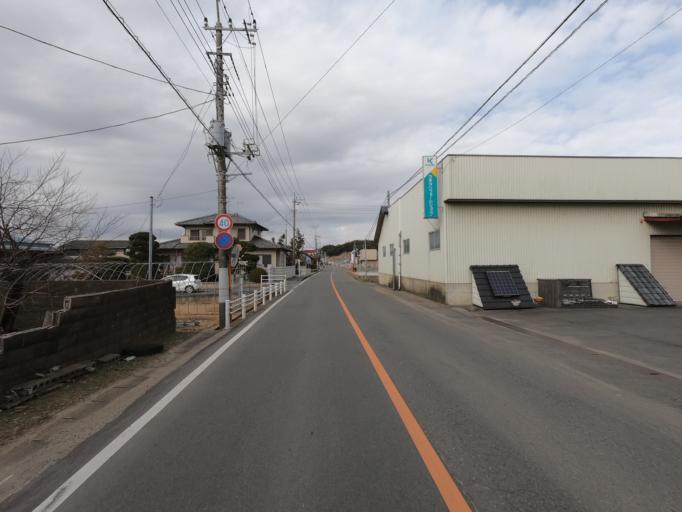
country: JP
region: Ibaraki
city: Inashiki
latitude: 36.0937
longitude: 140.4246
